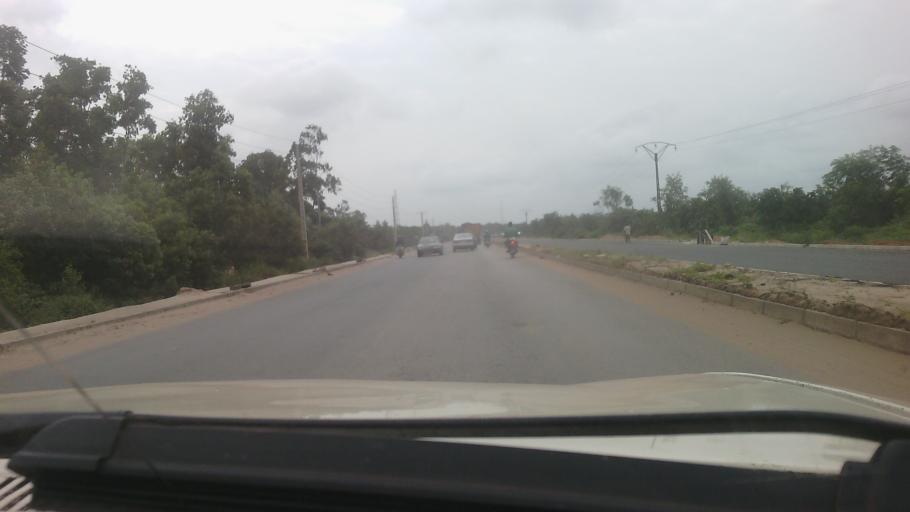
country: BJ
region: Atlantique
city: Ouidah
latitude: 6.3796
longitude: 2.1643
